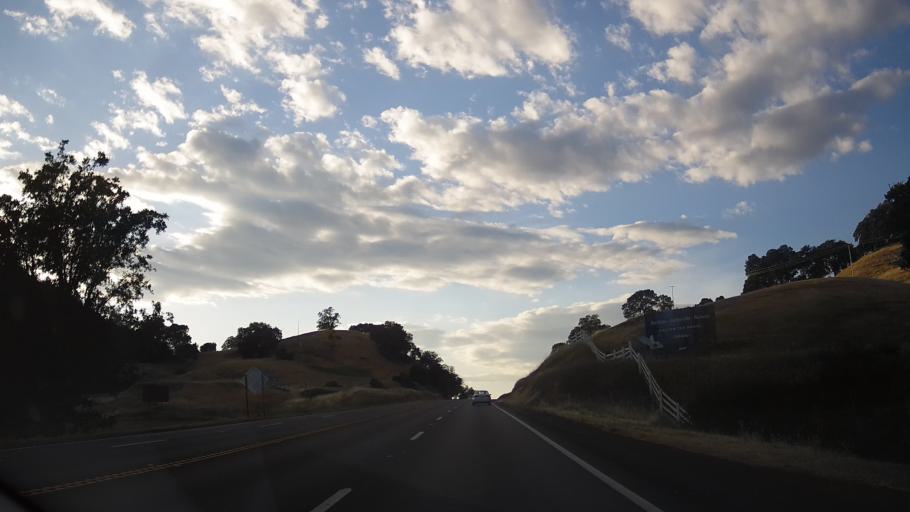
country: US
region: California
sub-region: Mendocino County
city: Talmage
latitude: 39.0258
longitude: -123.1373
